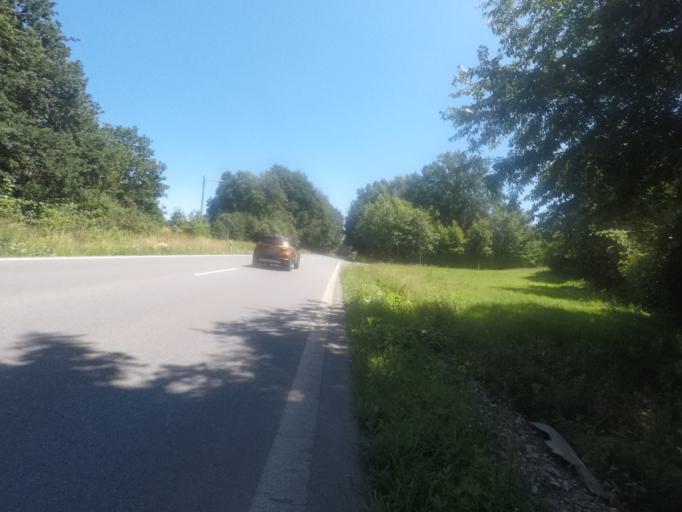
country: DE
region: North Rhine-Westphalia
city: Enger
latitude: 52.0999
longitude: 8.5634
